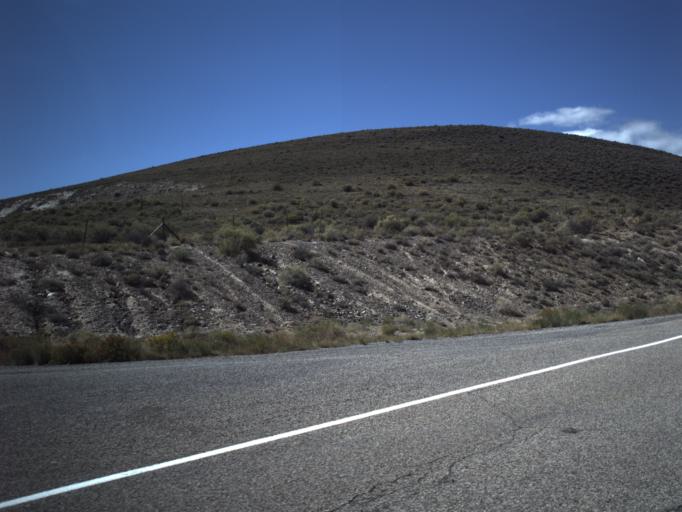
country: US
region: Utah
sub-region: Piute County
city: Junction
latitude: 38.2087
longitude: -112.2139
